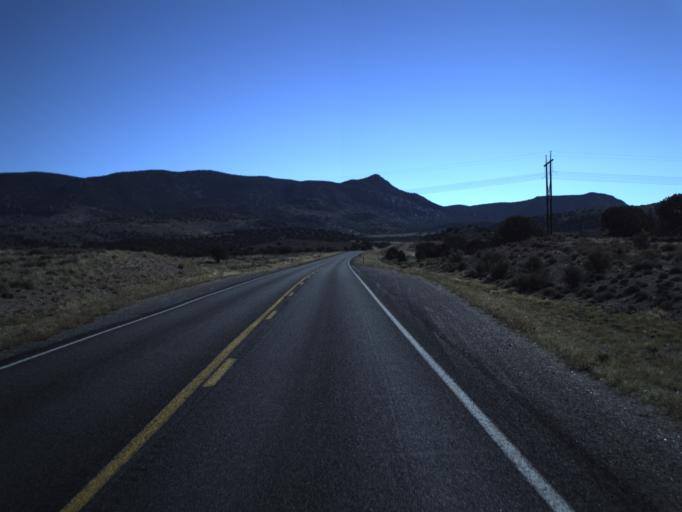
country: US
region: Utah
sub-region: Washington County
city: Enterprise
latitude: 37.6752
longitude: -113.5198
